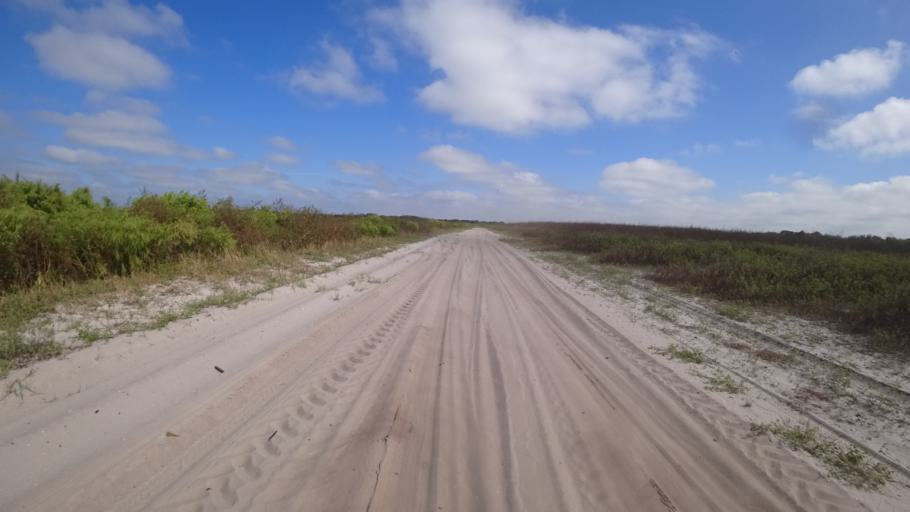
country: US
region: Florida
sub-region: DeSoto County
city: Arcadia
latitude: 27.2889
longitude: -82.0761
